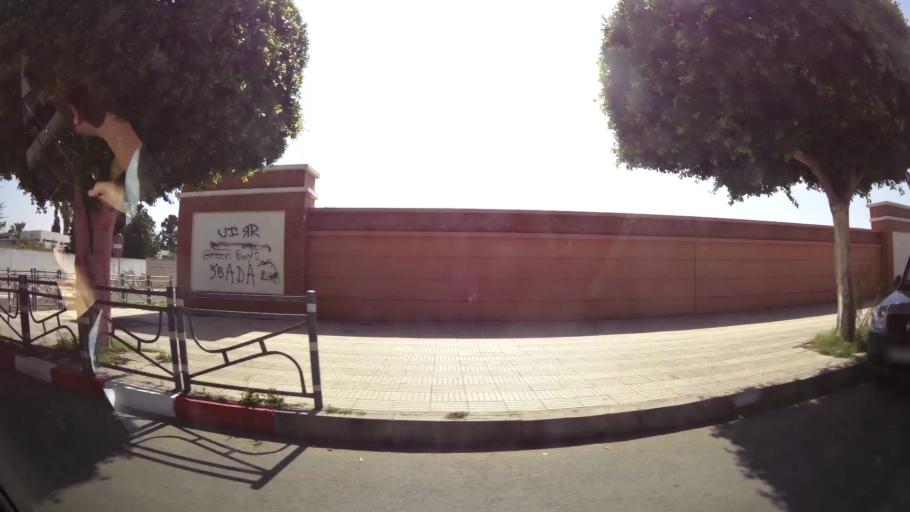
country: MA
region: Souss-Massa-Draa
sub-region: Inezgane-Ait Mellou
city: Inezgane
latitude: 30.3621
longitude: -9.5433
